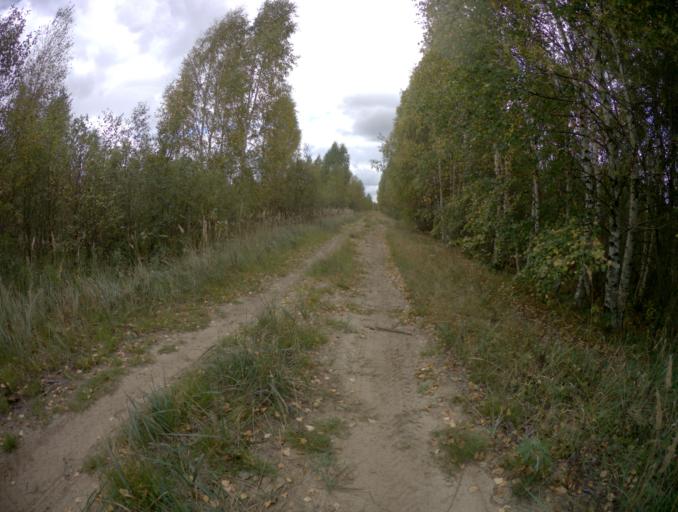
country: RU
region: Vladimir
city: Urshel'skiy
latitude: 55.7723
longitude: 40.1415
